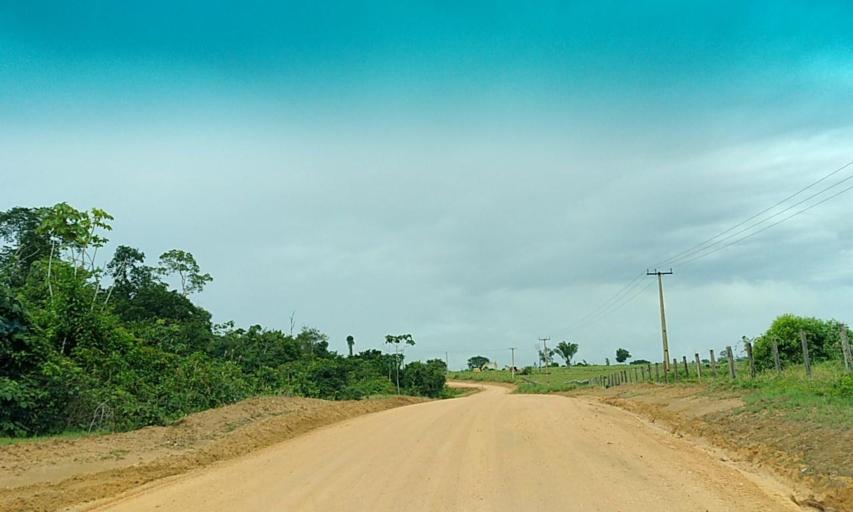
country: BR
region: Para
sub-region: Senador Jose Porfirio
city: Senador Jose Porfirio
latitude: -3.0592
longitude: -51.6706
